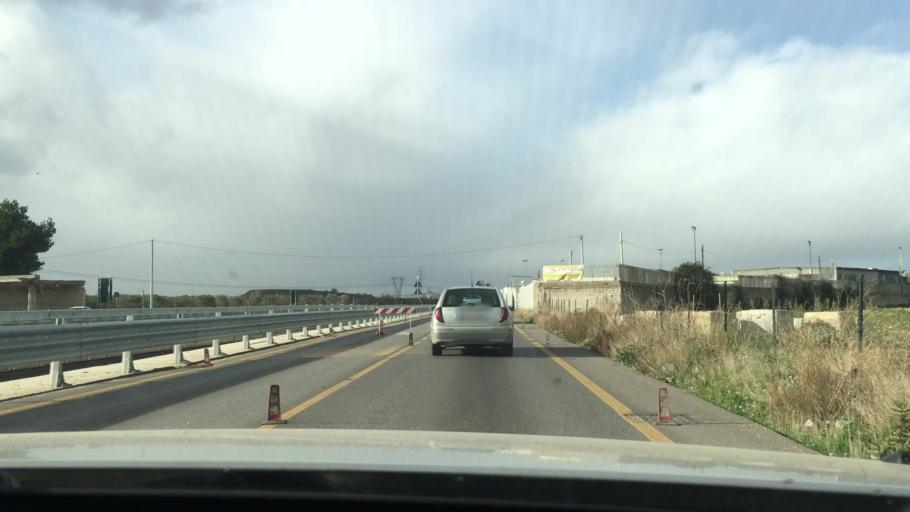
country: IT
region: Apulia
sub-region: Provincia di Bari
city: Bitetto
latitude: 41.0728
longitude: 16.7468
